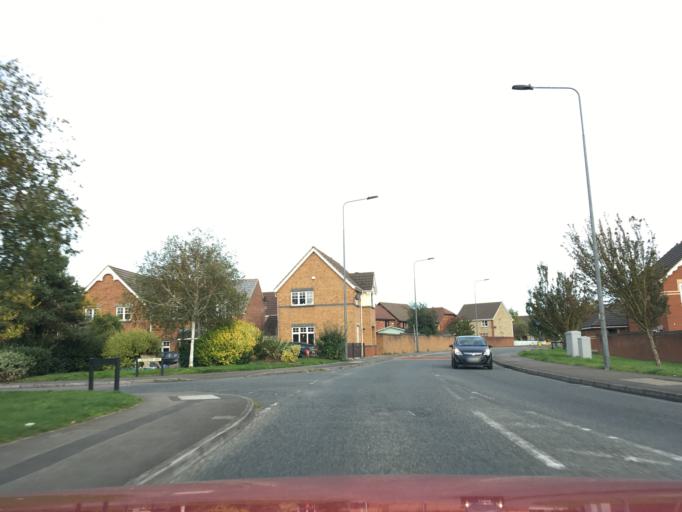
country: GB
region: England
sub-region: South Gloucestershire
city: Stoke Gifford
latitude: 51.5287
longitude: -2.5359
